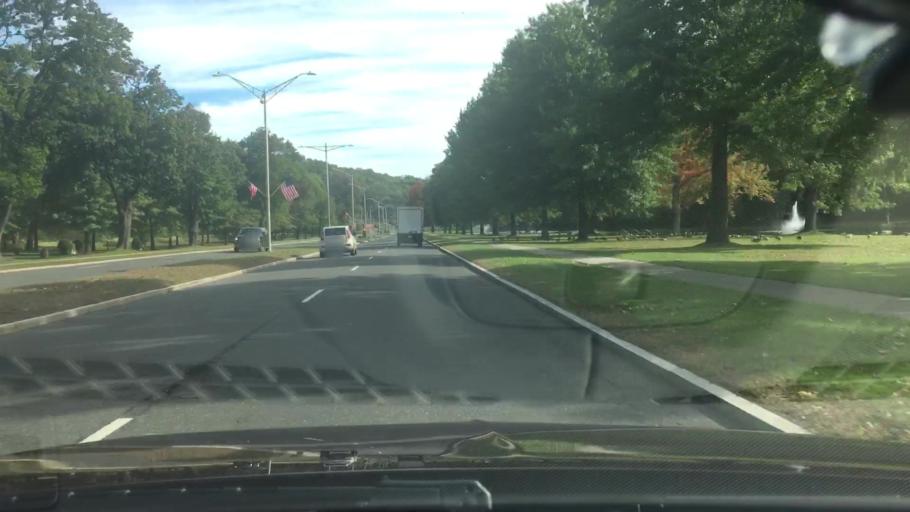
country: US
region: Connecticut
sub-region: Hartford County
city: Bristol
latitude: 41.6694
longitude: -72.9318
